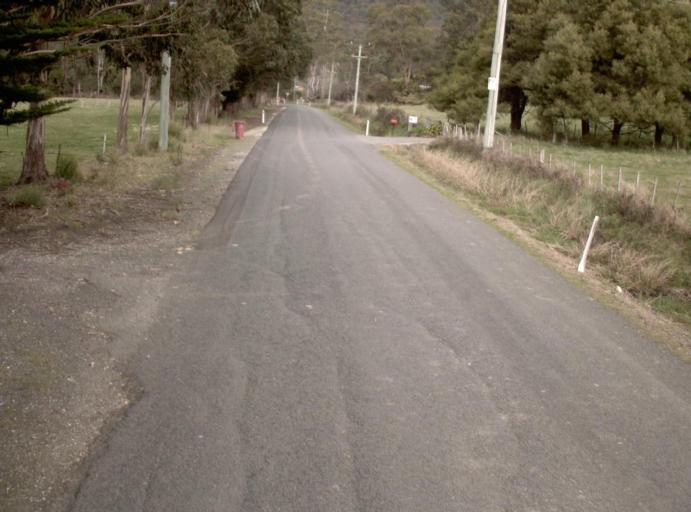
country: AU
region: Tasmania
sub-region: Launceston
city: Mayfield
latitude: -41.2665
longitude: 147.1606
